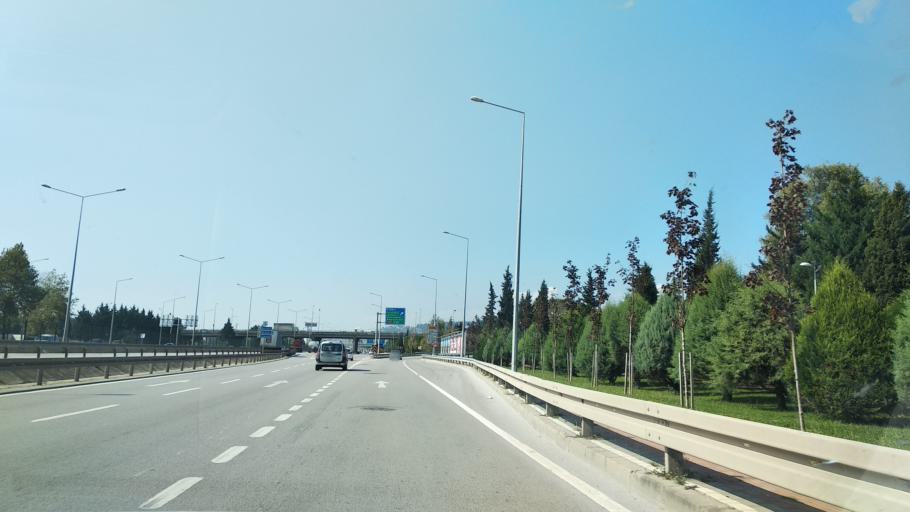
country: TR
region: Kocaeli
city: Kullar
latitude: 40.7614
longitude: 29.9699
